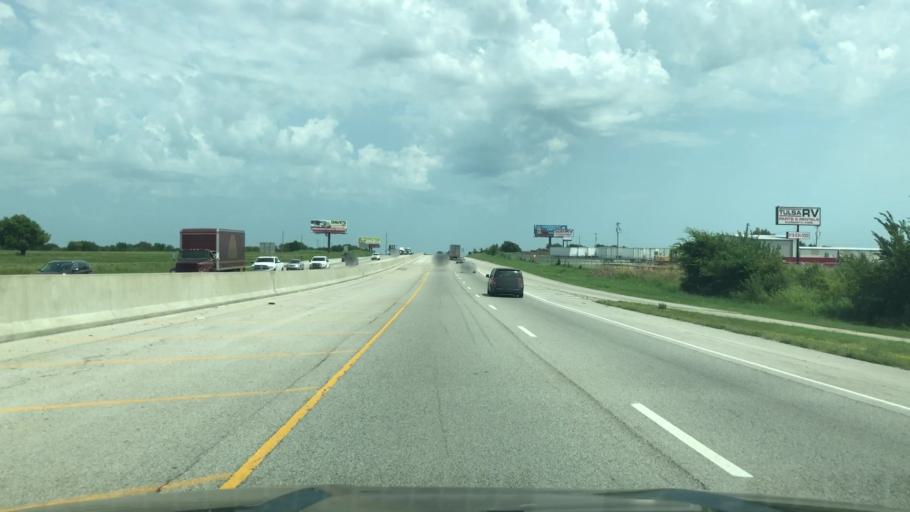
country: US
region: Oklahoma
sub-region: Rogers County
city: Catoosa
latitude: 36.1625
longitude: -95.7923
